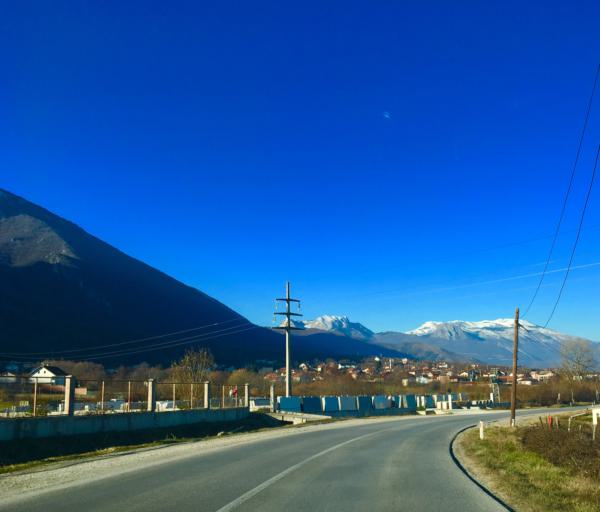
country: XK
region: Gjakova
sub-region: Komuna e Decanit
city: Strellc i Eperm
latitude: 42.5911
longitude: 20.2948
